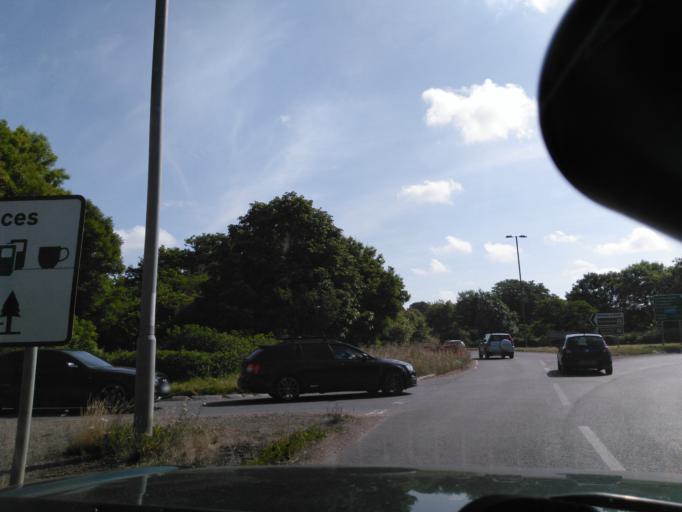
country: GB
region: England
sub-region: Hampshire
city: Romsey
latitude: 50.9542
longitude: -1.5351
